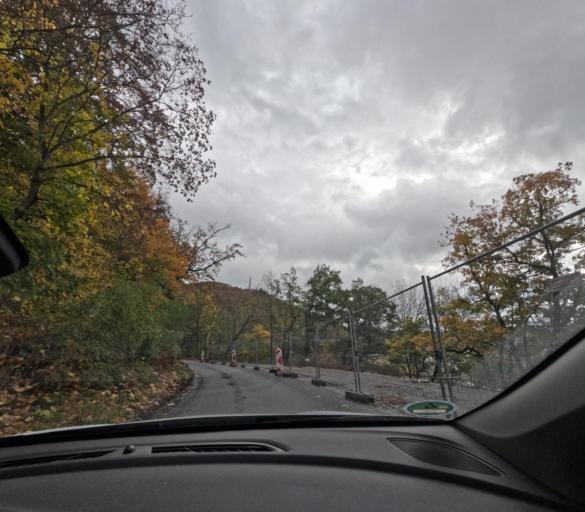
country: CZ
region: Karlovarsky
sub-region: Okres Karlovy Vary
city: Karlovy Vary
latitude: 50.2294
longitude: 12.8780
